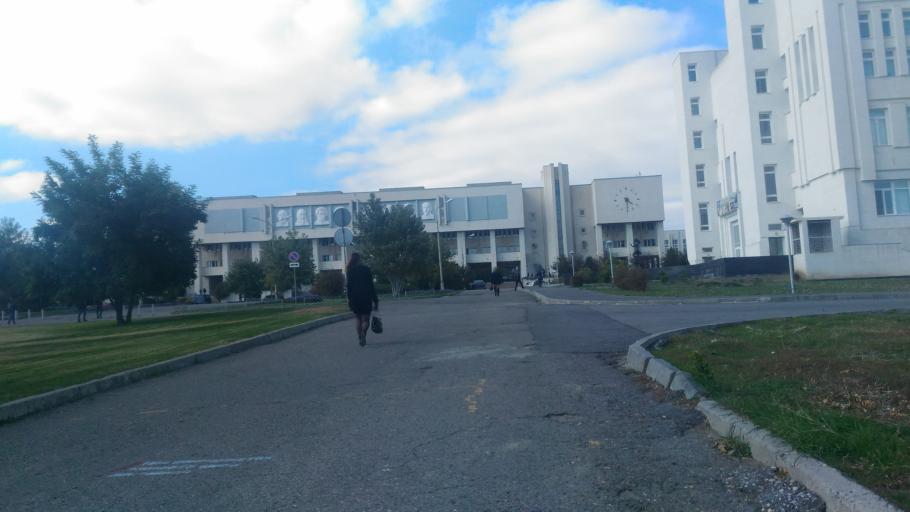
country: RU
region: Volgograd
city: Volgograd
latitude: 48.6417
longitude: 44.4252
